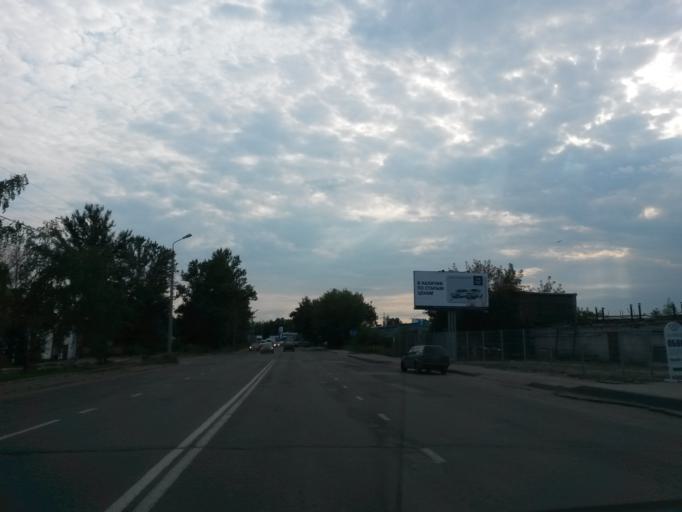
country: RU
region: Jaroslavl
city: Yaroslavl
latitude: 57.6171
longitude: 39.8446
